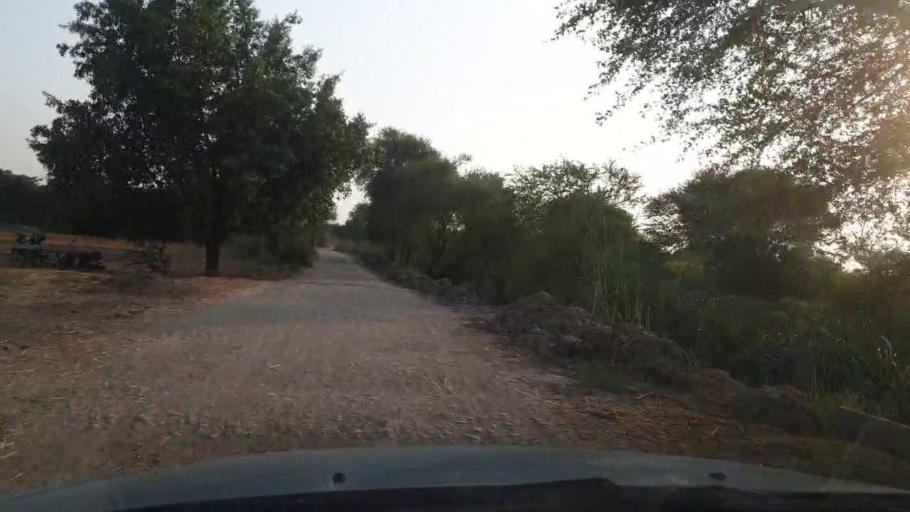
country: PK
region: Sindh
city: Tando Muhammad Khan
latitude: 25.0116
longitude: 68.4372
